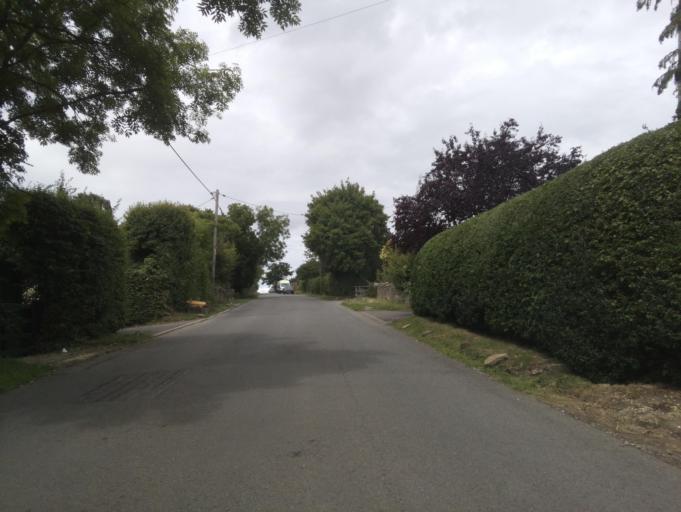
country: GB
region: England
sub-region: Wiltshire
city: Charlton
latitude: 51.5614
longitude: -2.0469
